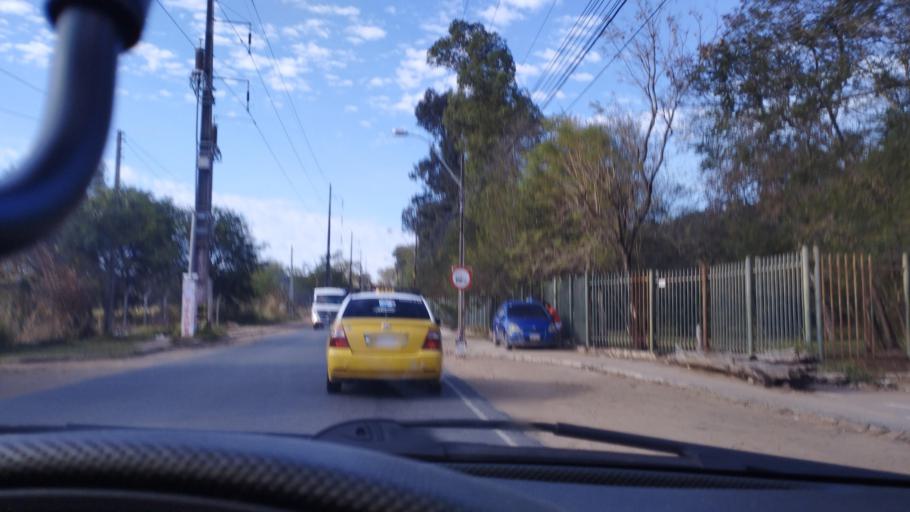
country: PY
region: Asuncion
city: Asuncion
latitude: -25.2495
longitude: -57.5794
